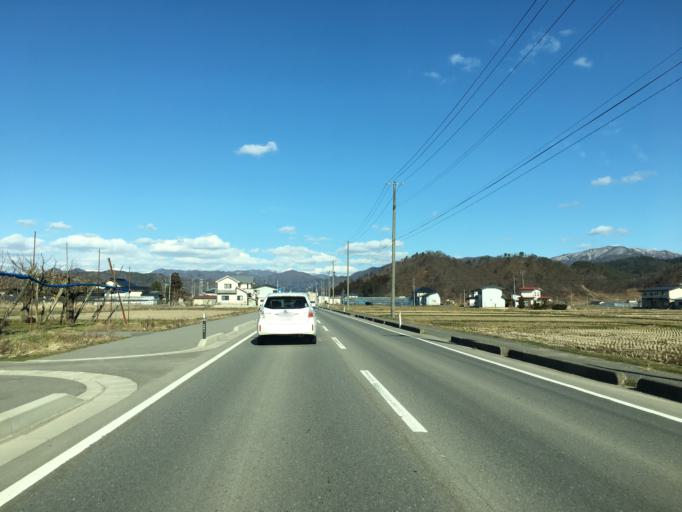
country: JP
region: Yamagata
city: Takahata
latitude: 37.9943
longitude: 140.1813
